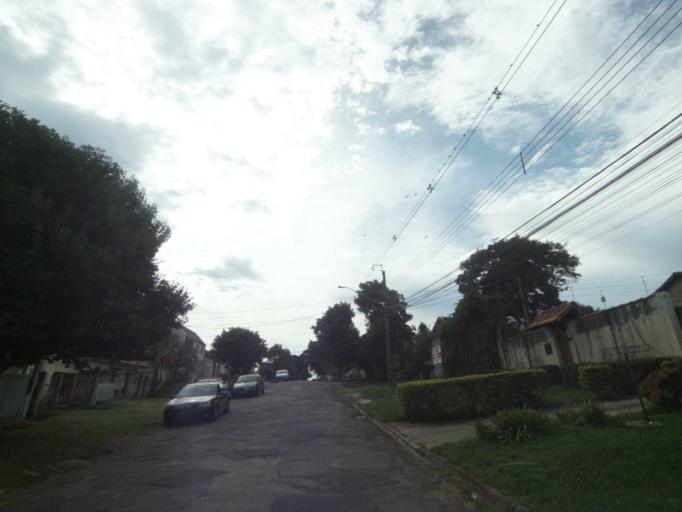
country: BR
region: Parana
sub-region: Pinhais
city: Pinhais
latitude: -25.4448
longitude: -49.2181
